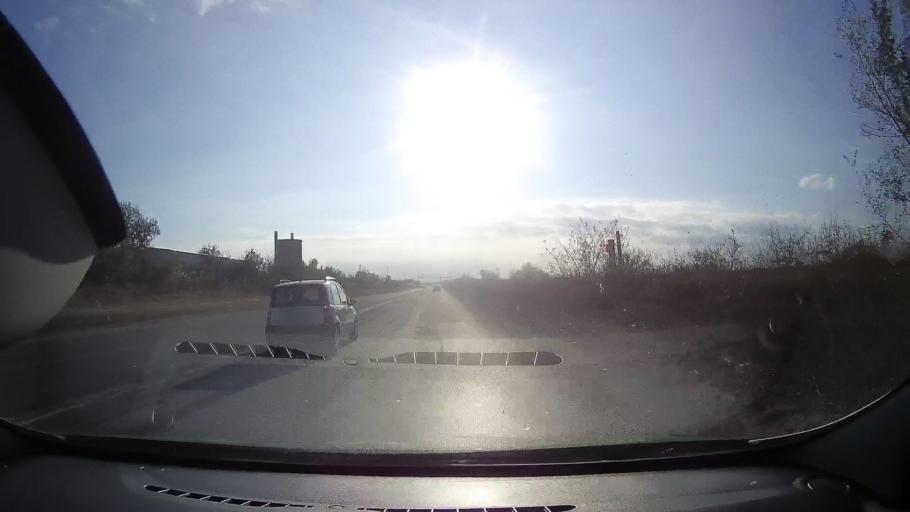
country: RO
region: Constanta
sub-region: Comuna Corbu
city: Corbu
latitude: 44.3500
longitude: 28.6471
